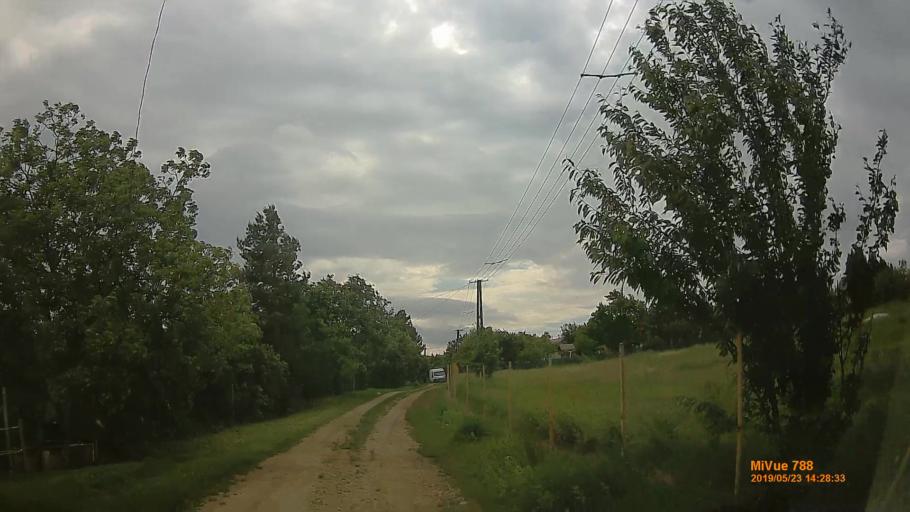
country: HU
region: Veszprem
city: Nemesvamos
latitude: 47.1059
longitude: 17.8523
